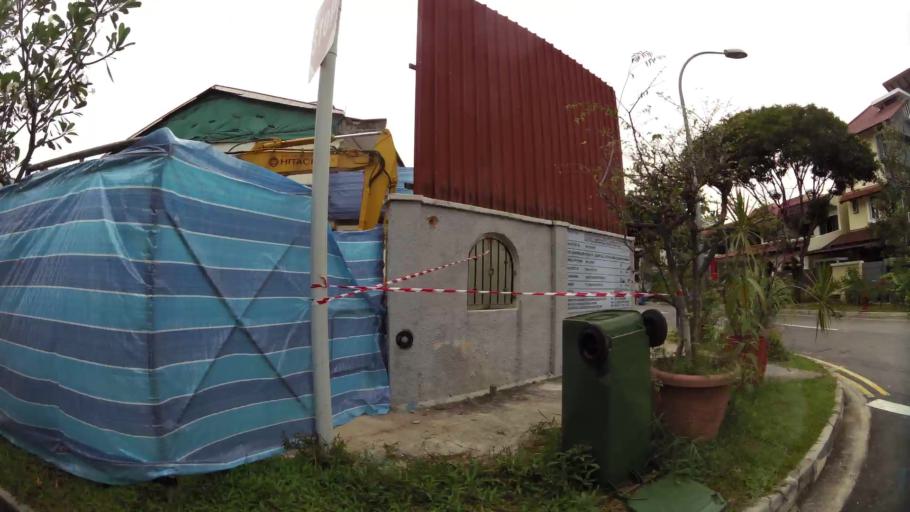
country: SG
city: Singapore
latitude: 1.3686
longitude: 103.8888
